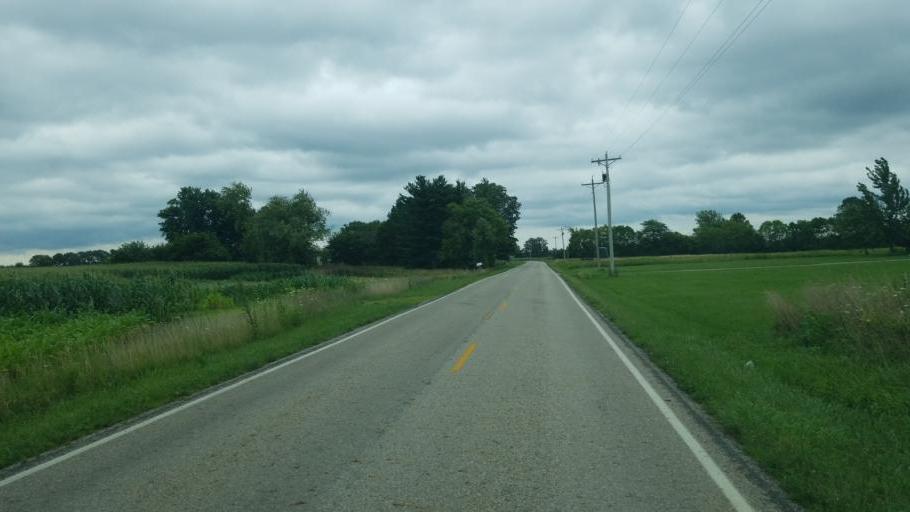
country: US
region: Ohio
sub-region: Pickaway County
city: Circleville
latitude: 39.6384
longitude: -82.9801
